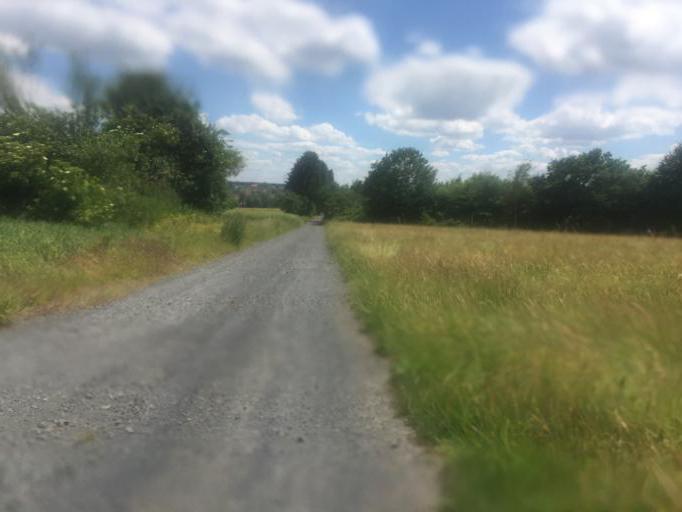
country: DE
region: Rheinland-Pfalz
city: Steinefrenz
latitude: 50.4671
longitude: 7.9280
